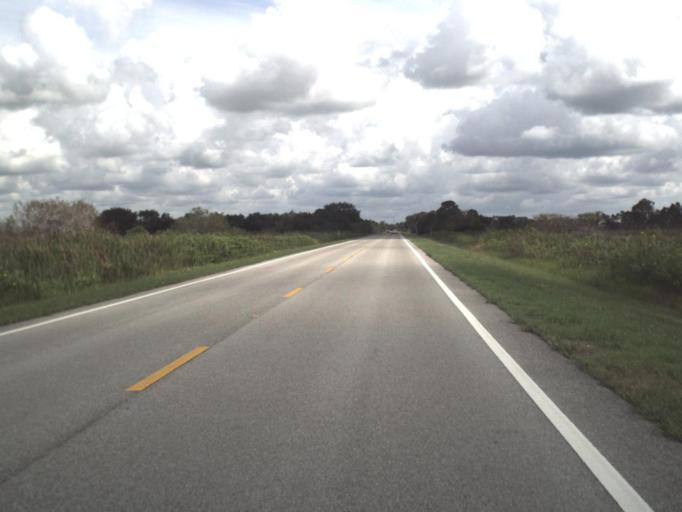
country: US
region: Florida
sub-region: Sarasota County
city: Warm Mineral Springs
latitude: 27.2107
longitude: -82.2577
